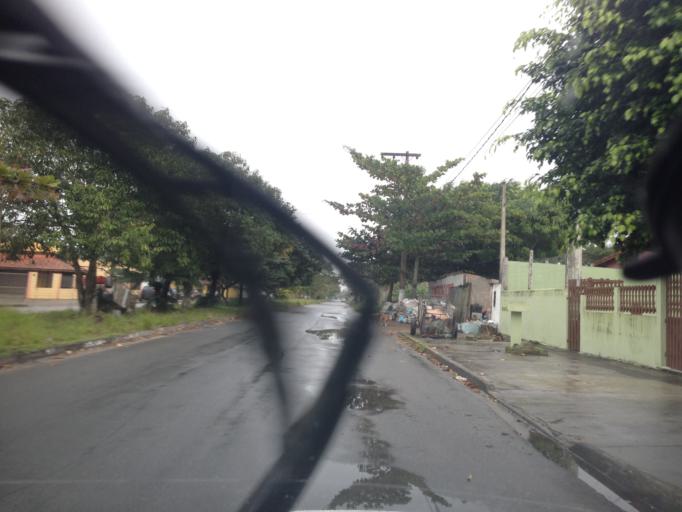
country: BR
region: Sao Paulo
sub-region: Itanhaem
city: Itanhaem
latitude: -24.2247
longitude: -46.8654
